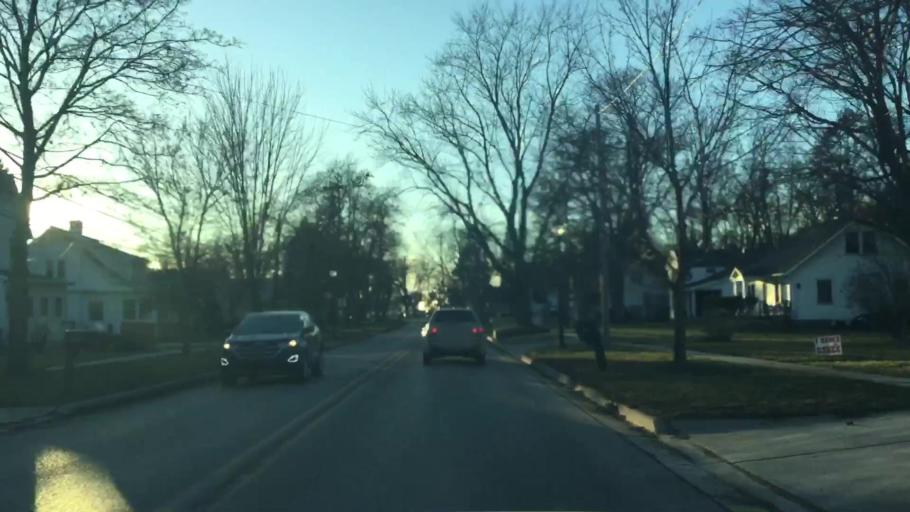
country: US
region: Michigan
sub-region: Genesee County
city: Linden
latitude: 42.8142
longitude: -83.7852
